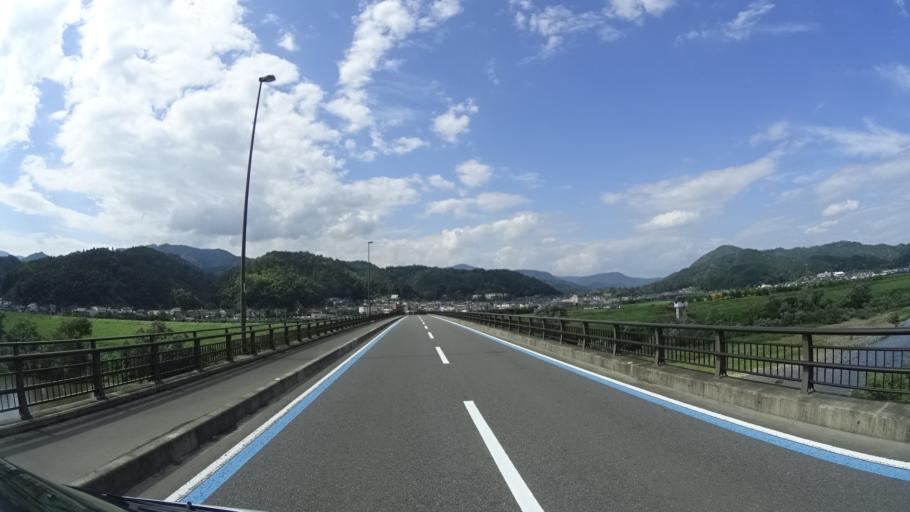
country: JP
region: Kyoto
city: Fukuchiyama
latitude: 35.3834
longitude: 135.1475
